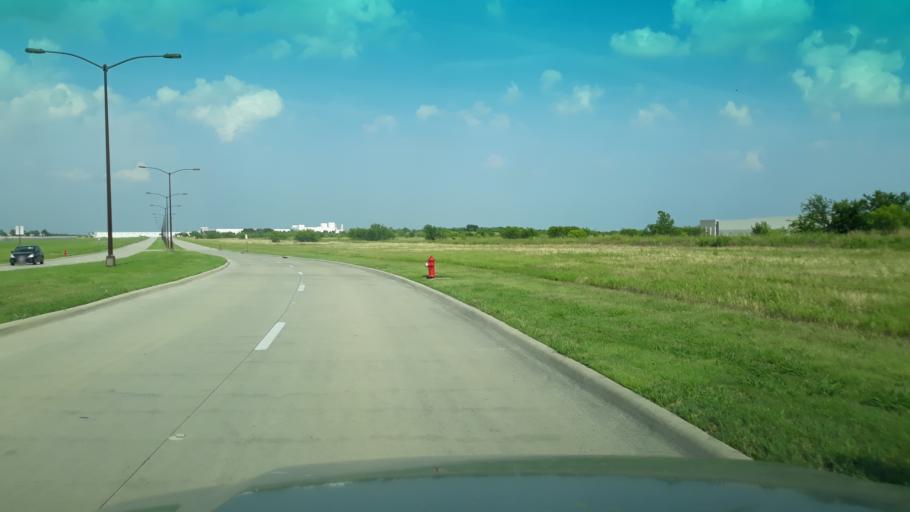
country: US
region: Texas
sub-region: Tarrant County
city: Euless
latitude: 32.8704
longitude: -97.0328
